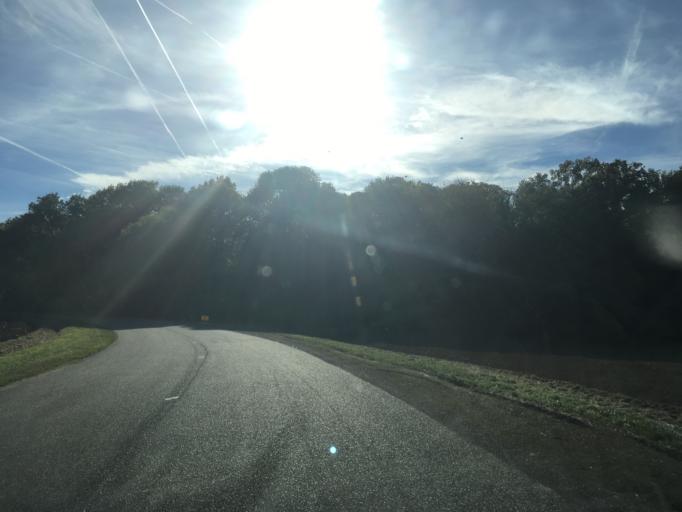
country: FR
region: Haute-Normandie
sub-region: Departement de l'Eure
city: Saint-Marcel
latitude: 49.0575
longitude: 1.4207
